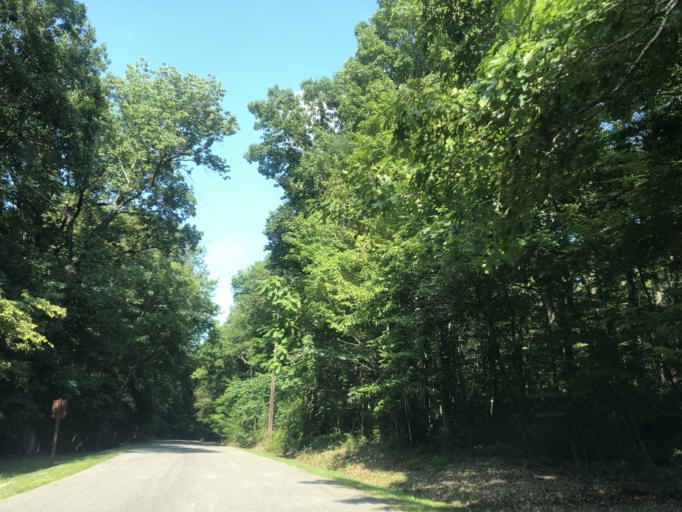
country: US
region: Tennessee
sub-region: Wilson County
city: Green Hill
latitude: 36.1372
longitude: -86.5998
